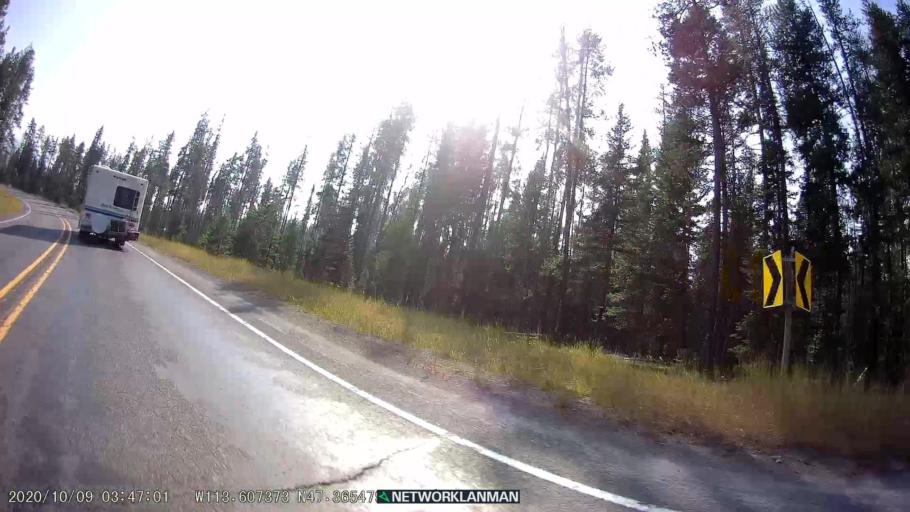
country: US
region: Montana
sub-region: Missoula County
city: Seeley Lake
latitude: 47.3653
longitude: -113.6070
